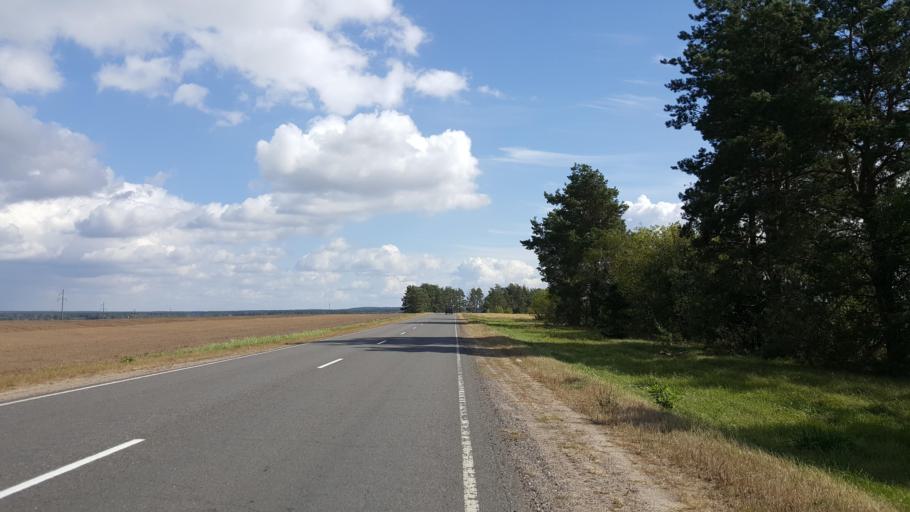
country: BY
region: Brest
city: Kamyanyets
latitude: 52.4031
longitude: 23.8547
